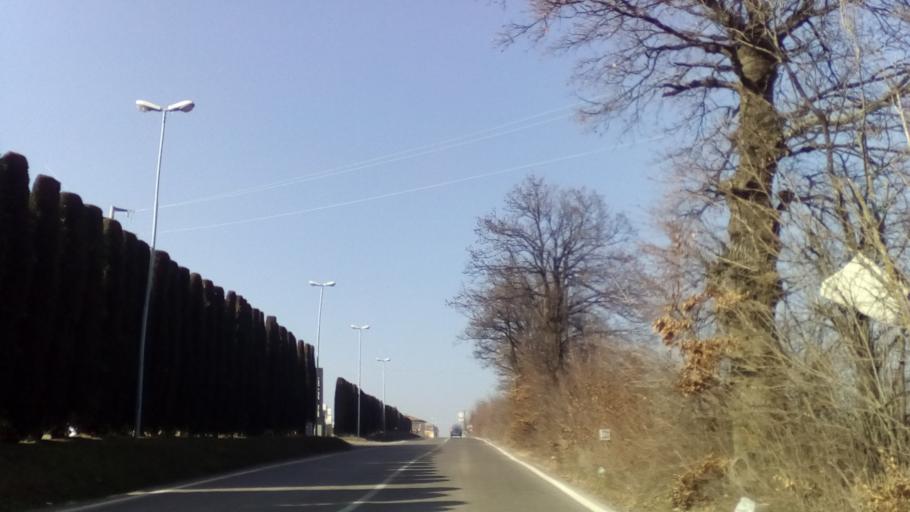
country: IT
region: Emilia-Romagna
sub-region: Provincia di Modena
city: Sant'Antonio
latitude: 44.3785
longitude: 10.8238
